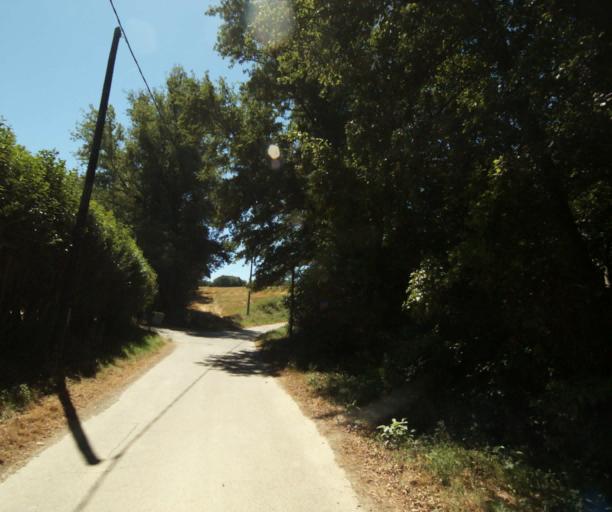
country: FR
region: Midi-Pyrenees
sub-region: Departement de la Haute-Garonne
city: Castanet-Tolosan
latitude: 43.5060
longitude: 1.4939
